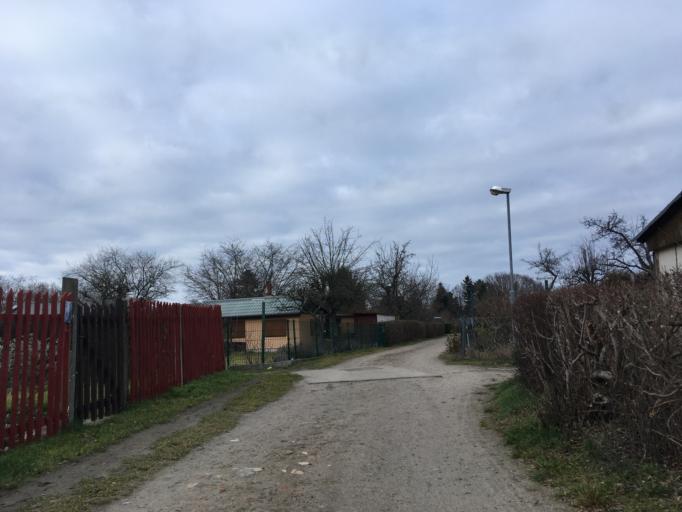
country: DE
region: Berlin
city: Niederschonhausen
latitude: 52.5777
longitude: 13.3915
